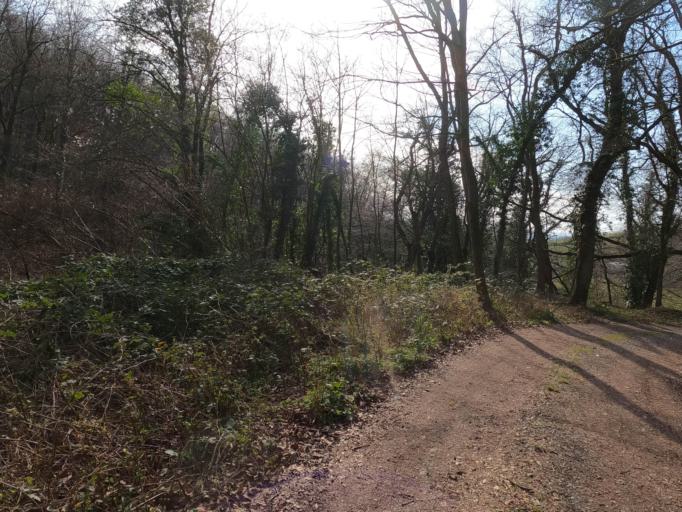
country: DE
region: Baden-Wuerttemberg
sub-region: Karlsruhe Region
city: Laudenbach
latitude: 49.6240
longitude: 8.6562
